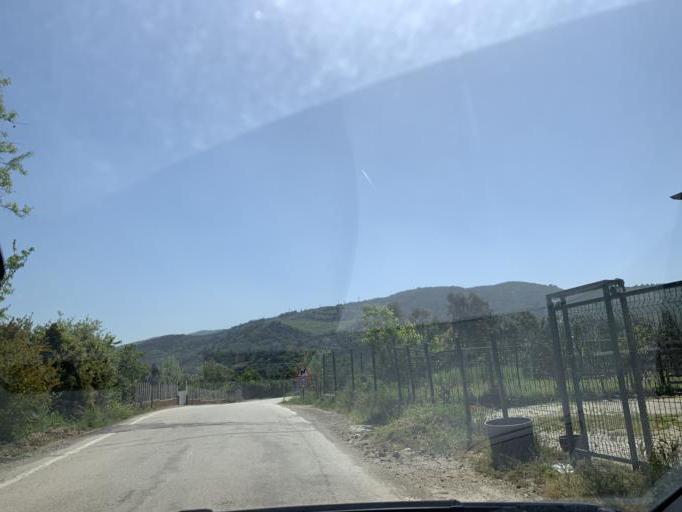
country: TR
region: Bursa
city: Niluefer
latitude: 40.3551
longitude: 28.9625
